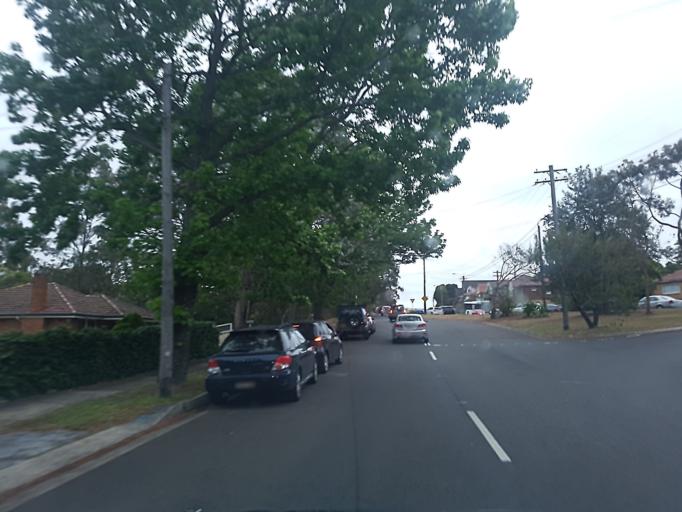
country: AU
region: New South Wales
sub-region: Ku-ring-gai
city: Roseville Chase
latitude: -33.7823
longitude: 151.1958
